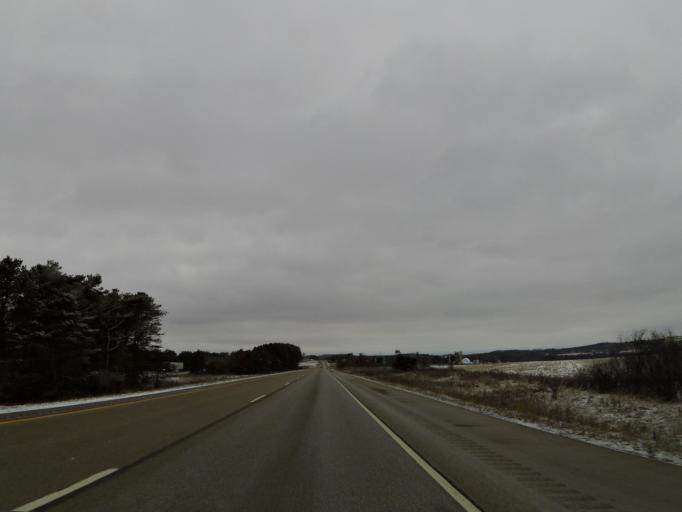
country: US
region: Wisconsin
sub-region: Trempealeau County
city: Osseo
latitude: 44.5273
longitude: -91.1492
